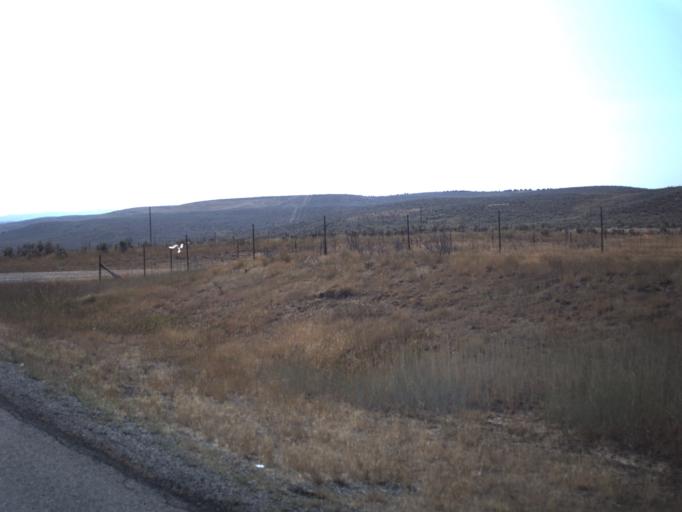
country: US
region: Wyoming
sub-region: Uinta County
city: Evanston
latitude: 41.1185
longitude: -111.1905
